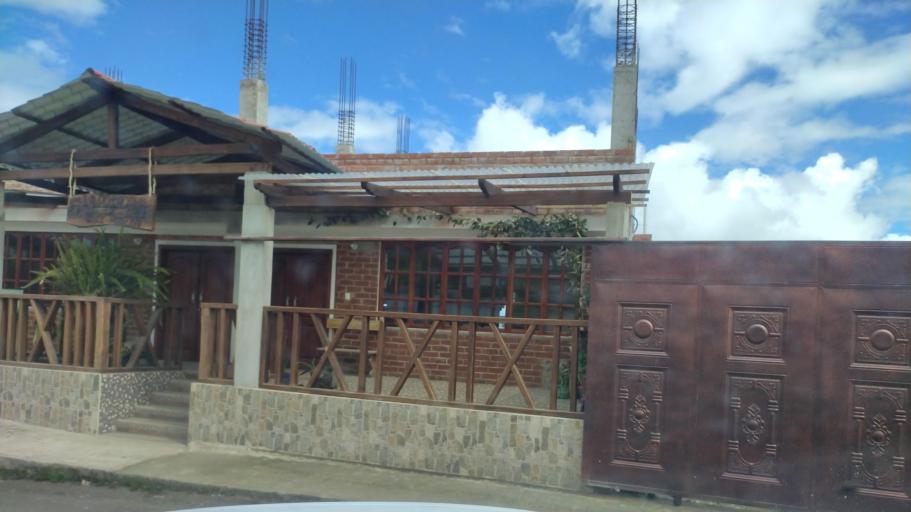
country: EC
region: Chimborazo
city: Guano
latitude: -1.6567
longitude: -78.5664
